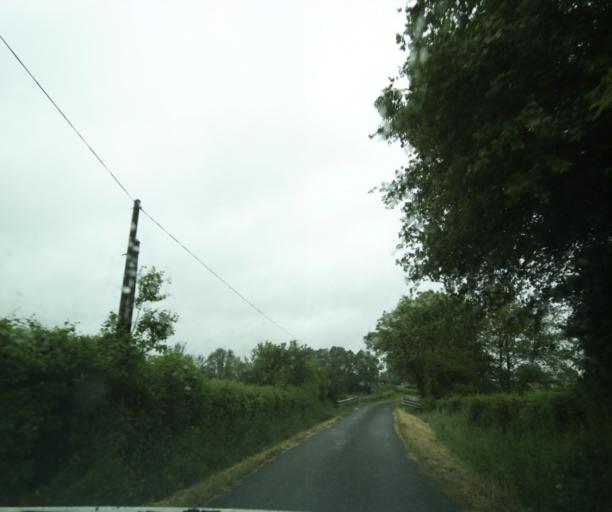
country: FR
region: Bourgogne
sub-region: Departement de Saone-et-Loire
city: Palinges
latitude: 46.5421
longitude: 4.2108
